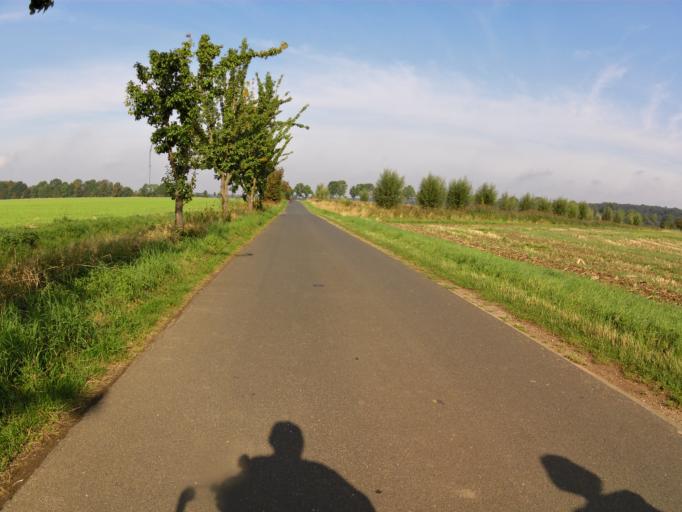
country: DE
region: Lower Saxony
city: Langwedel
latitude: 52.9699
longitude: 9.1652
